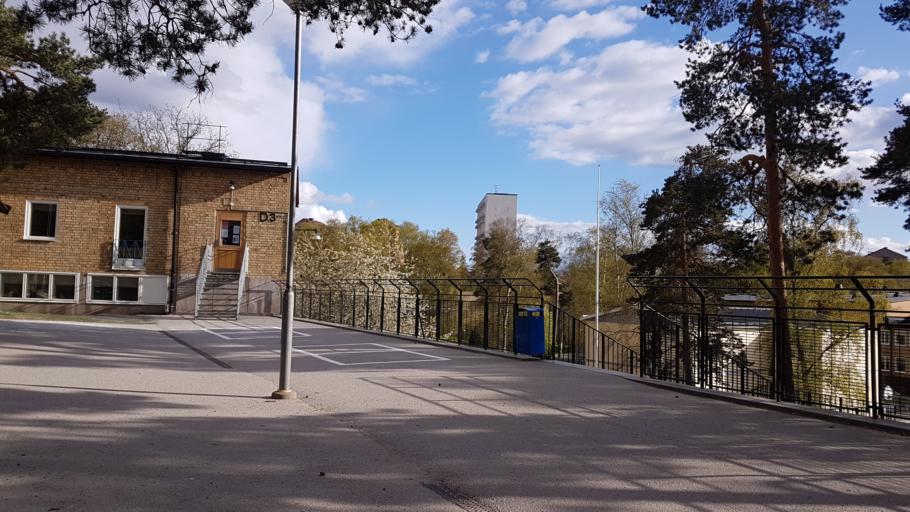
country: SE
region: Stockholm
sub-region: Nacka Kommun
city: Nacka
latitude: 59.2941
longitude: 18.1180
